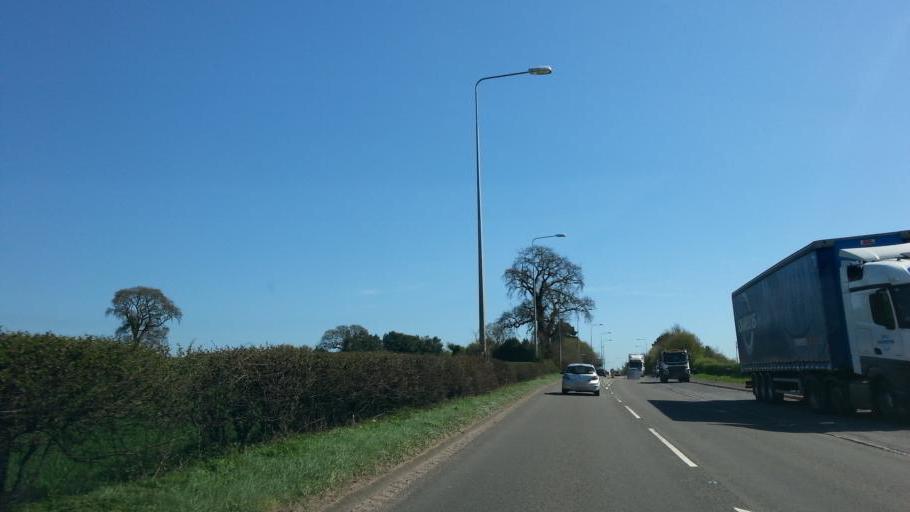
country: GB
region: England
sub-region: Staffordshire
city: Wheaton Aston
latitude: 52.6941
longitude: -2.2518
